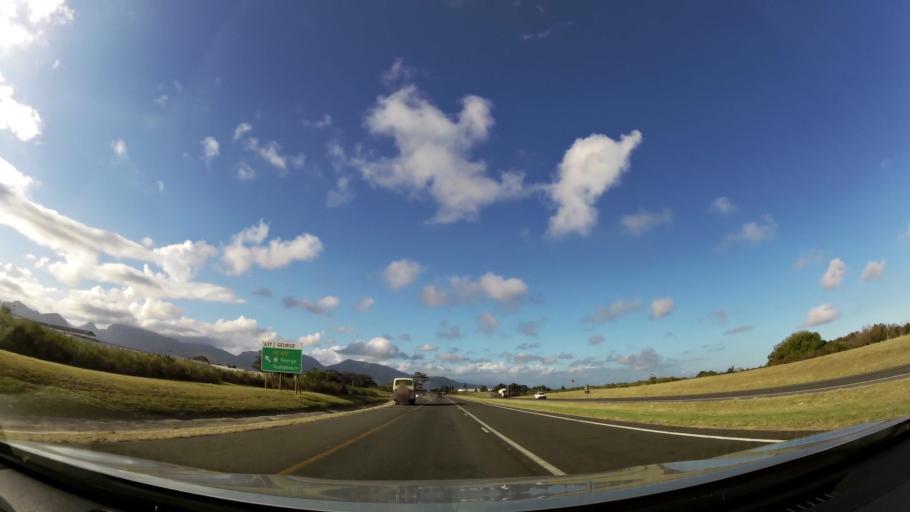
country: ZA
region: Western Cape
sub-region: Eden District Municipality
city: George
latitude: -33.9886
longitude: 22.5037
